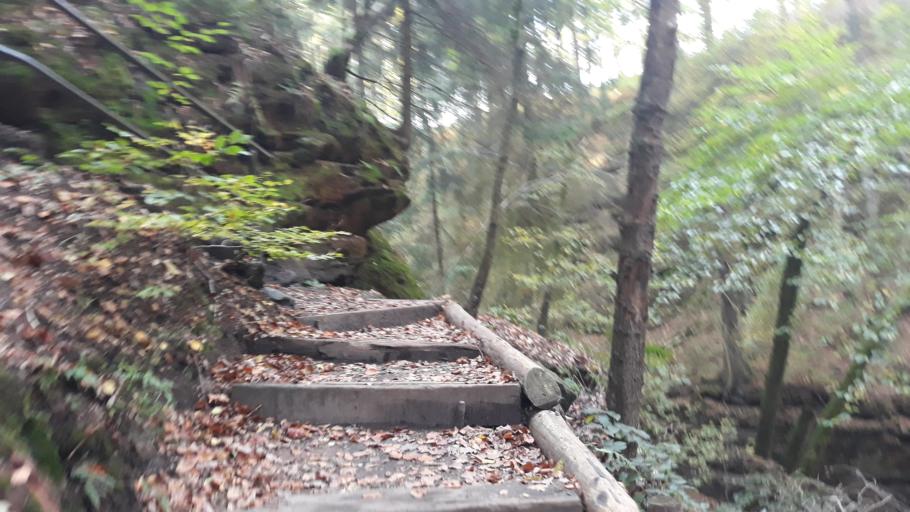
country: DE
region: Saxony
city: Stadt Wehlen
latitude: 50.9670
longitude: 14.0271
